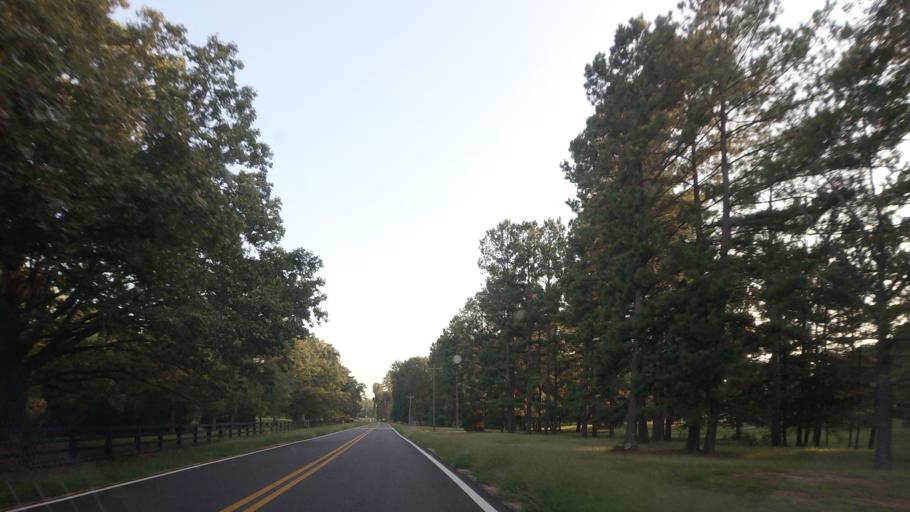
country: US
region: Georgia
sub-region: Bibb County
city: West Point
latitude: 32.9050
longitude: -83.8231
